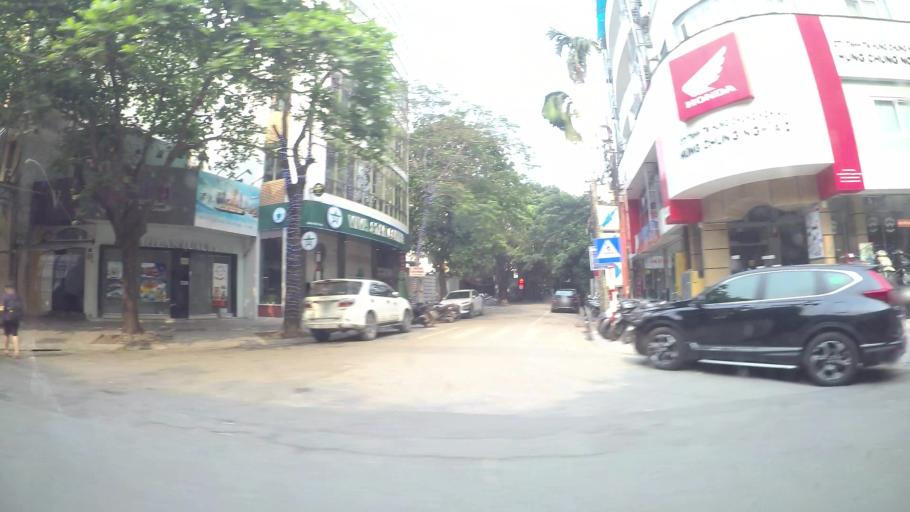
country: VN
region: Ha Noi
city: Hai BaTrung
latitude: 21.0096
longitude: 105.8490
